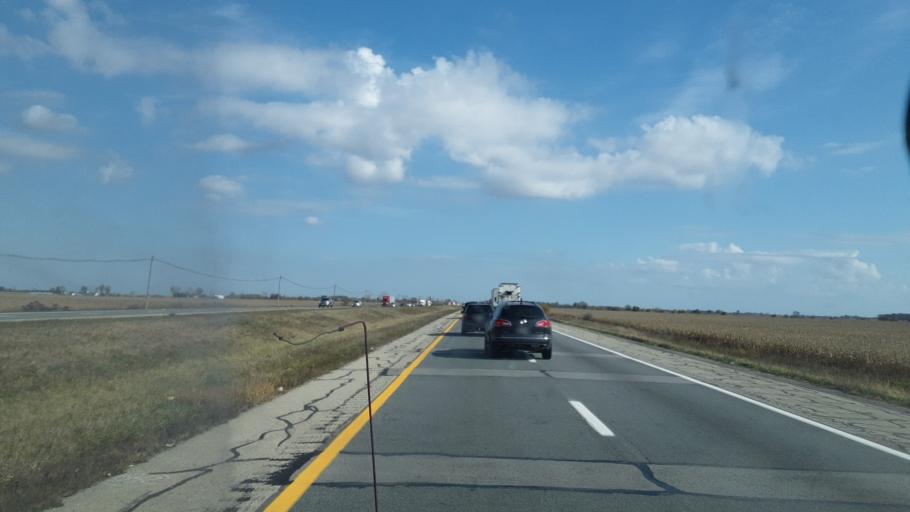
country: US
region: Ohio
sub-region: Fayette County
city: Jeffersonville
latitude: 39.6711
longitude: -83.5013
